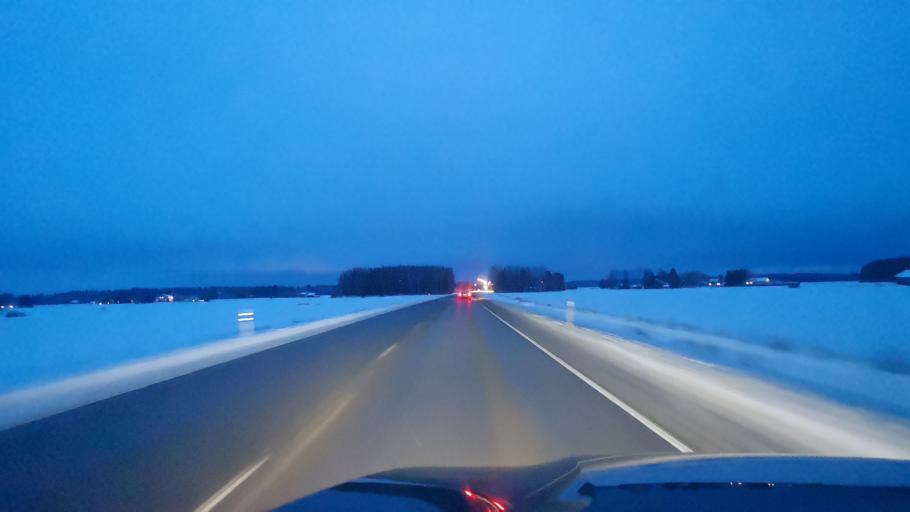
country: FI
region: Varsinais-Suomi
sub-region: Loimaa
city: Loimaa
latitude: 60.8800
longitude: 23.0778
